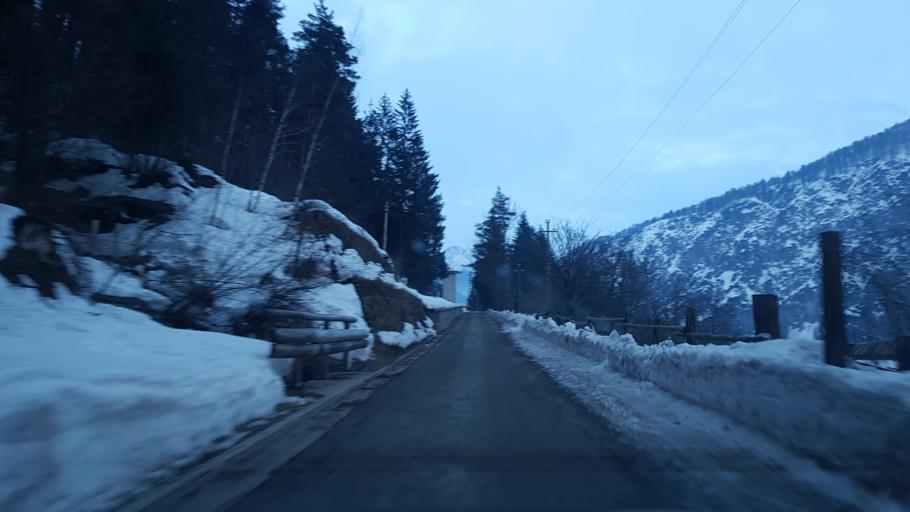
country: IT
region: Friuli Venezia Giulia
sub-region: Provincia di Udine
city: Malborghetto
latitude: 46.5135
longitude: 13.4736
